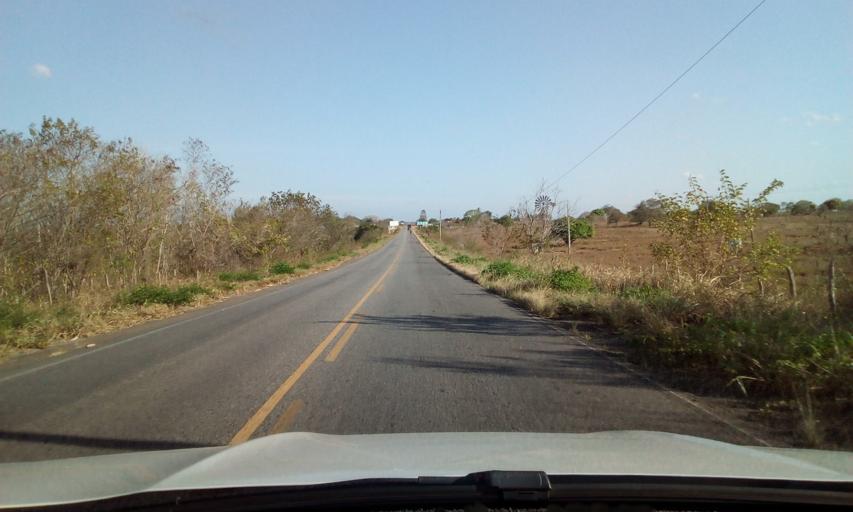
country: BR
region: Paraiba
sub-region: Guarabira
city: Guarabira
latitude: -6.9237
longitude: -35.4444
